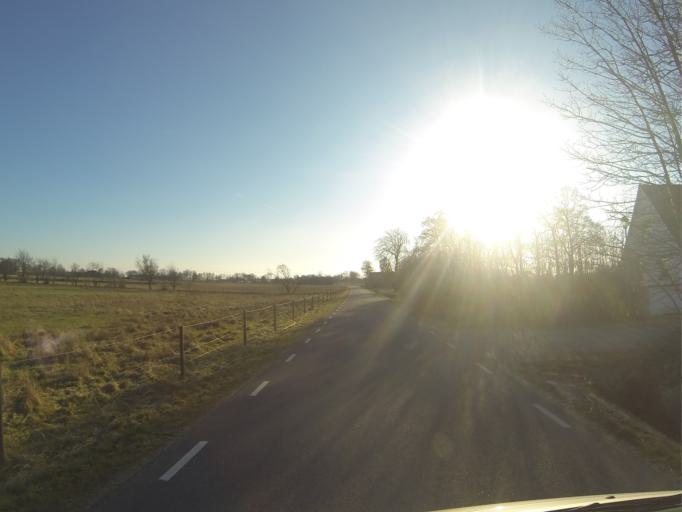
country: SE
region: Skane
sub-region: Hoors Kommun
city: Loberod
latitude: 55.7569
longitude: 13.4746
